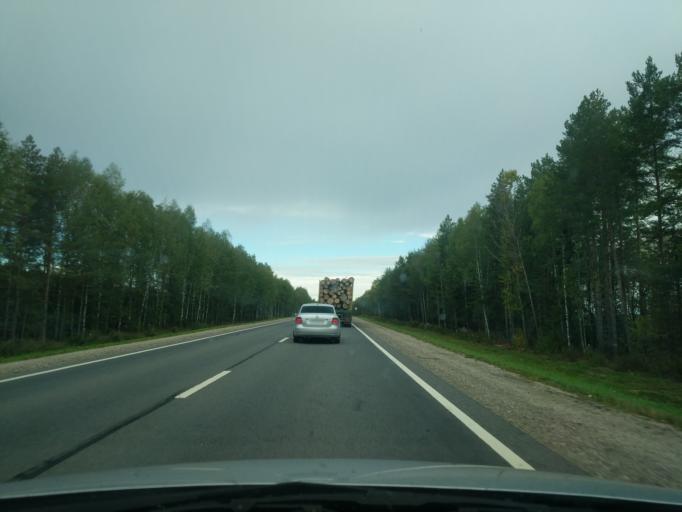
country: RU
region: Kostroma
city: Ostrovskoye
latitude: 57.8069
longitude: 42.3040
